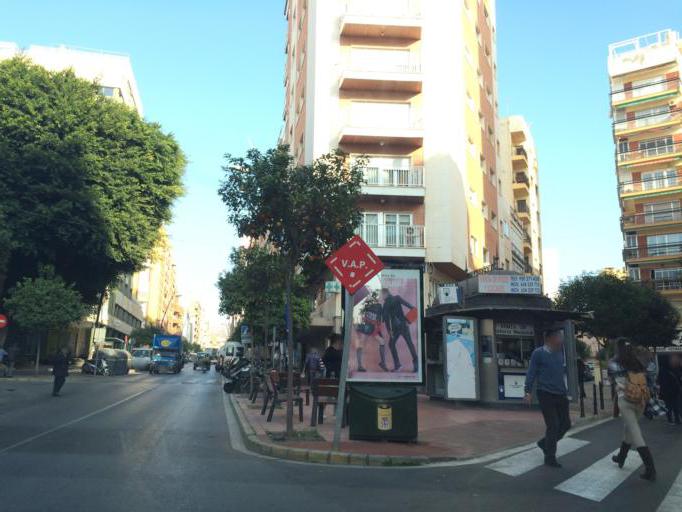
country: ES
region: Andalusia
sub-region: Provincia de Almeria
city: Almeria
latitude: 36.8427
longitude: -2.4641
